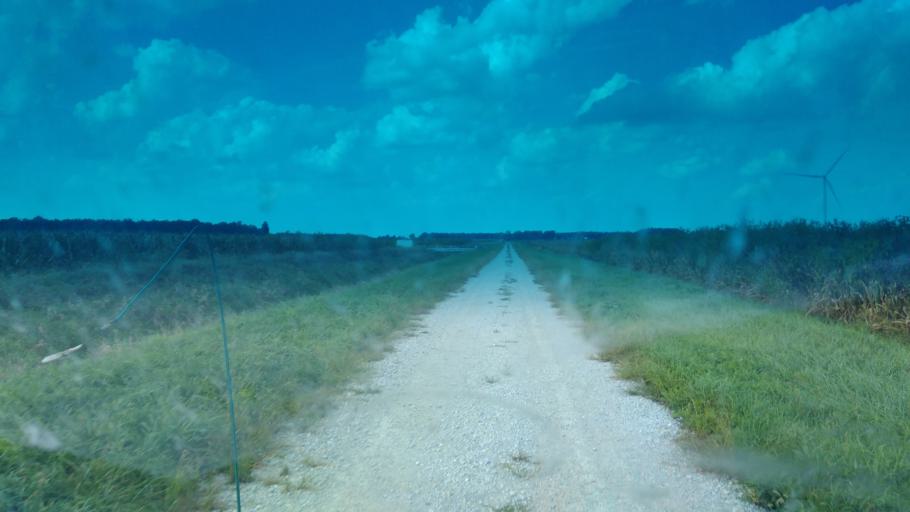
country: US
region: Ohio
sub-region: Hancock County
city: Arlington
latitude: 40.7950
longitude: -83.6899
